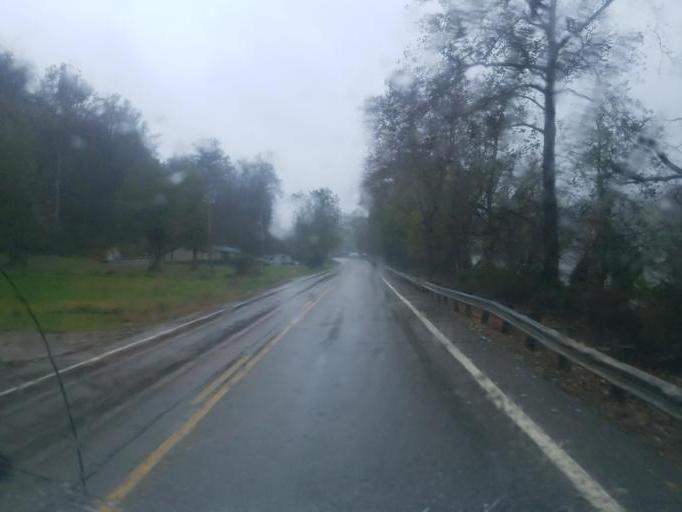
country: US
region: Ohio
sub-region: Morgan County
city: McConnelsville
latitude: 39.6884
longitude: -81.8861
